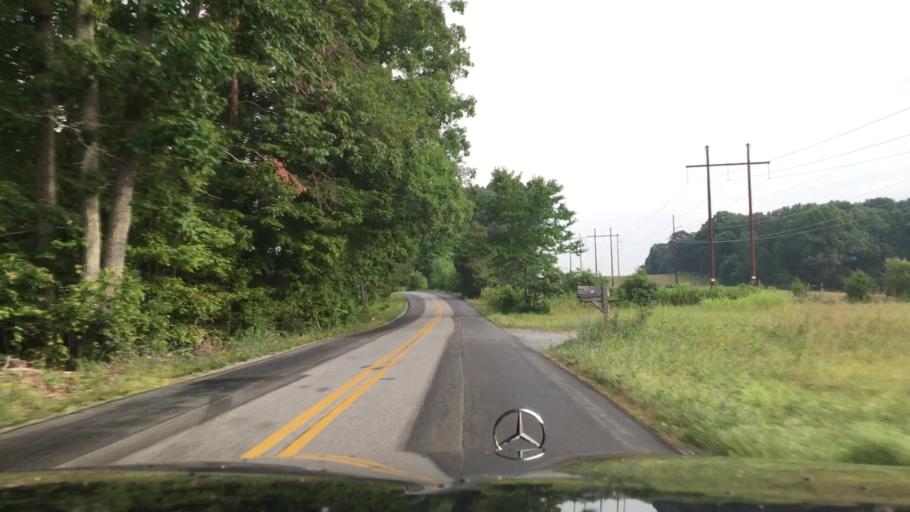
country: US
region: Virginia
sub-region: Campbell County
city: Timberlake
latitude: 37.2727
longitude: -79.3115
